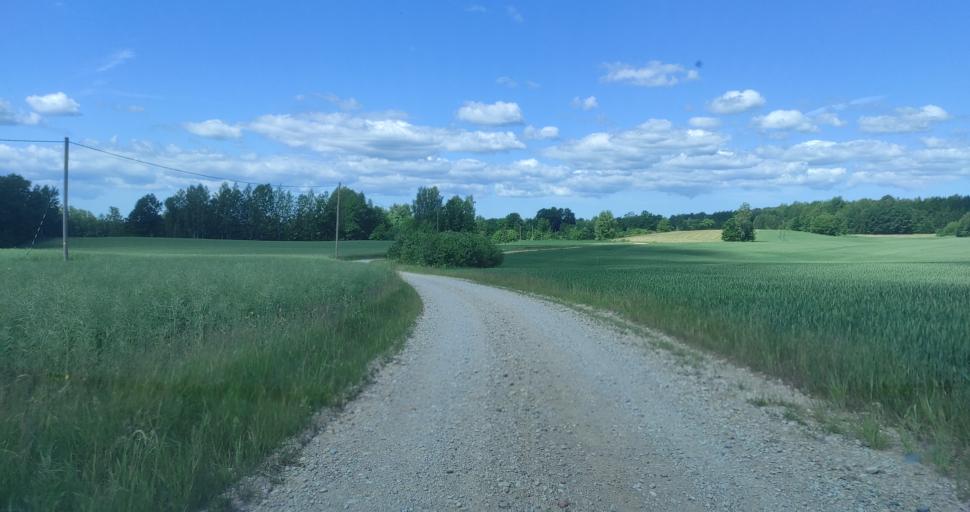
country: LV
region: Alsunga
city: Alsunga
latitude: 56.8768
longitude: 21.7164
